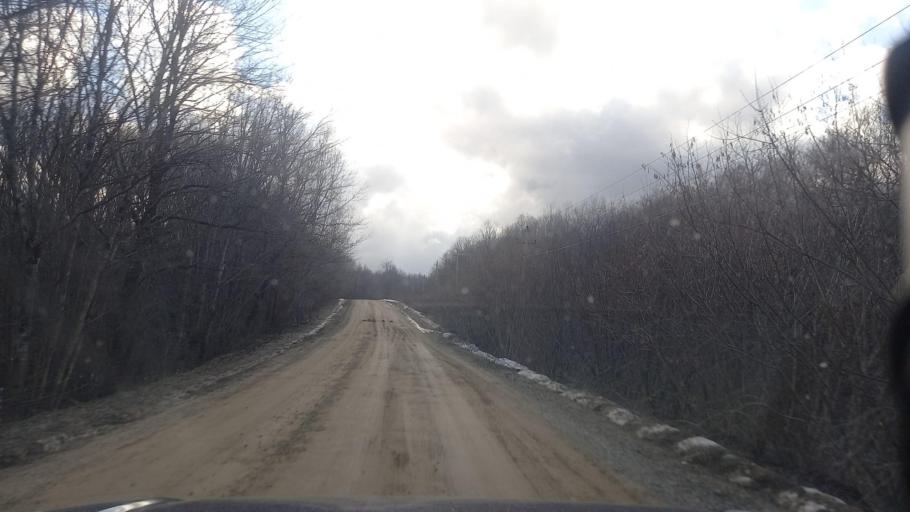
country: RU
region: Krasnodarskiy
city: Smolenskaya
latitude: 44.5841
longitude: 38.8093
